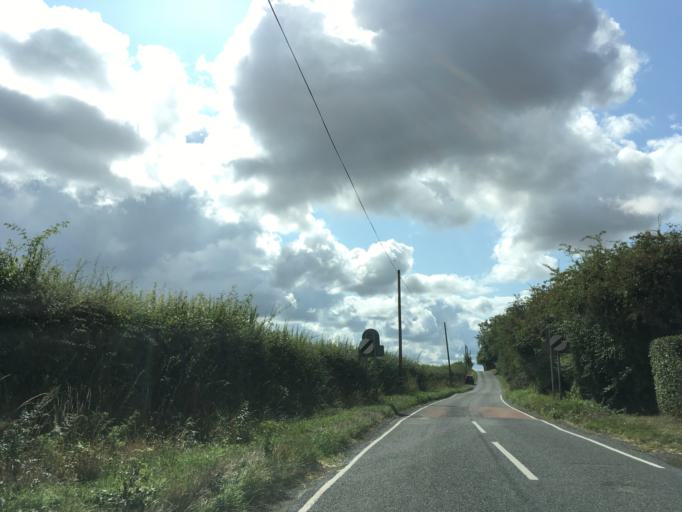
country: GB
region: England
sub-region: Hampshire
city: Kings Worthy
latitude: 51.1635
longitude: -1.3791
